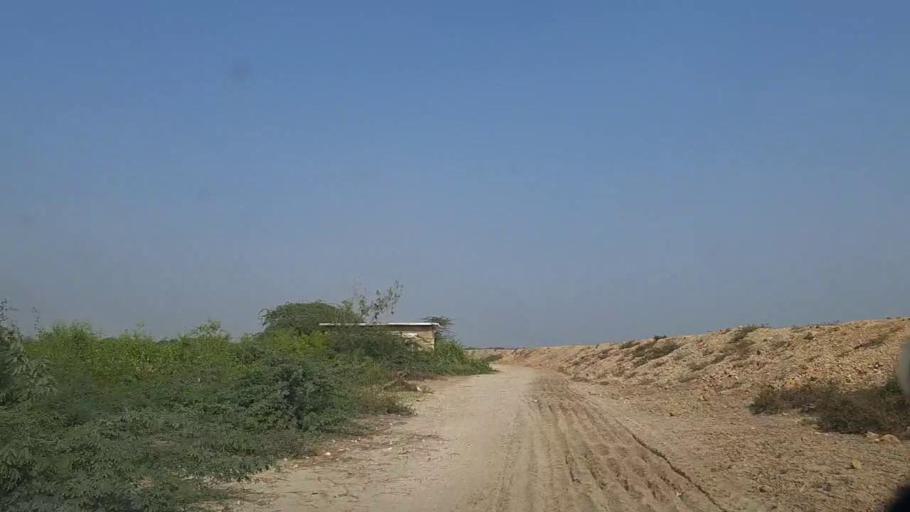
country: PK
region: Sindh
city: Thatta
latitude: 24.6558
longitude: 67.9266
